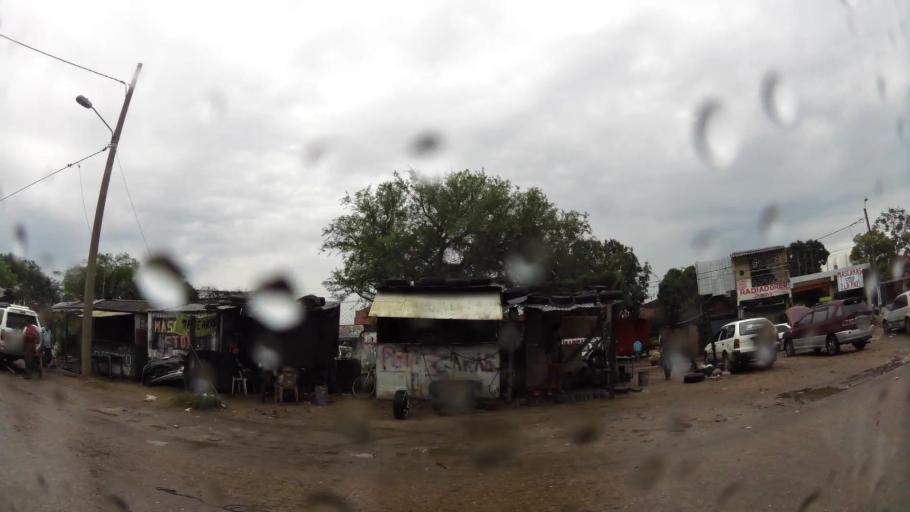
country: BO
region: Santa Cruz
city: Santa Cruz de la Sierra
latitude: -17.8101
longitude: -63.1955
